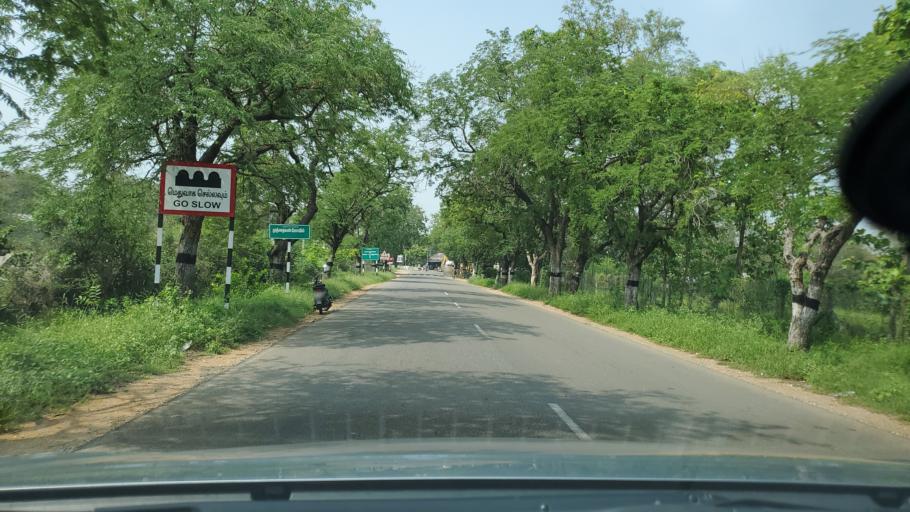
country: IN
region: Tamil Nadu
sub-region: Erode
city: Chennimalai
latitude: 11.1873
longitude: 77.6111
